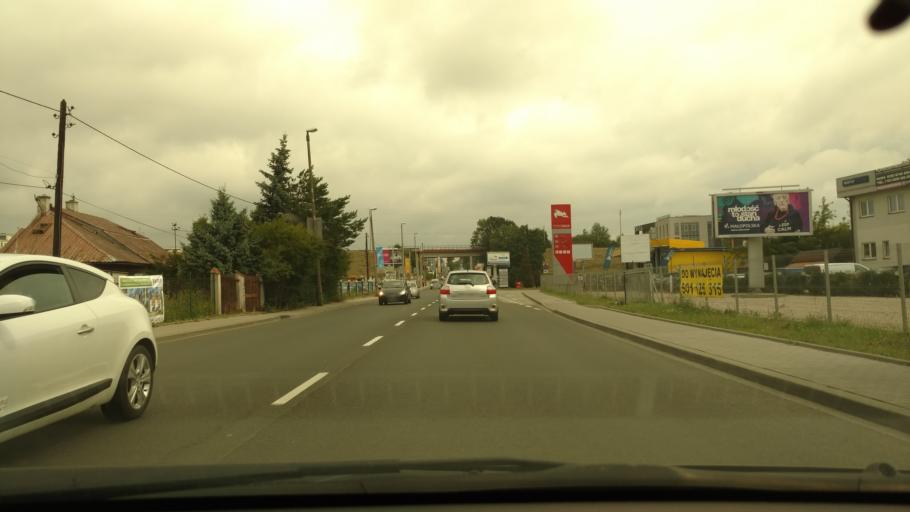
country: PL
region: Lesser Poland Voivodeship
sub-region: Krakow
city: Krakow
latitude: 50.0942
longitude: 19.9611
